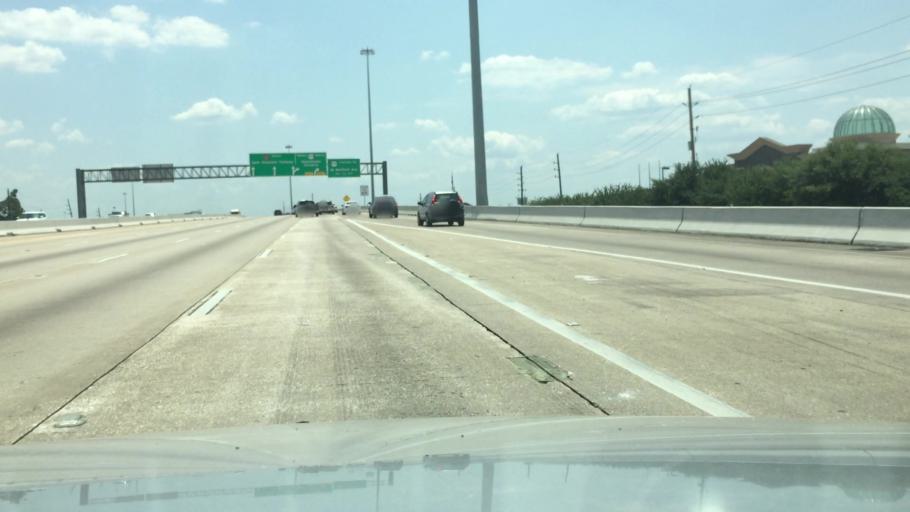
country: US
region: Texas
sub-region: Fort Bend County
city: Meadows Place
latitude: 29.6775
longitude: -95.5600
